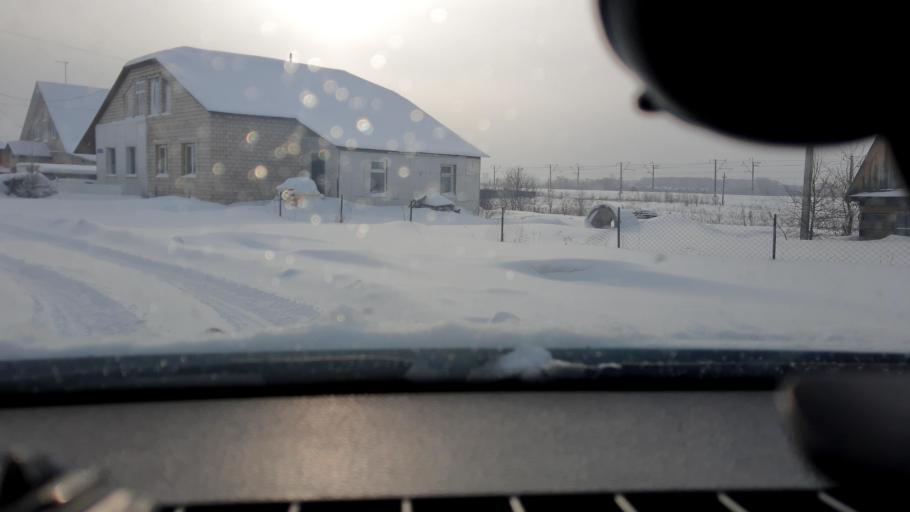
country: RU
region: Bashkortostan
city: Ufa
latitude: 54.6087
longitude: 55.8886
